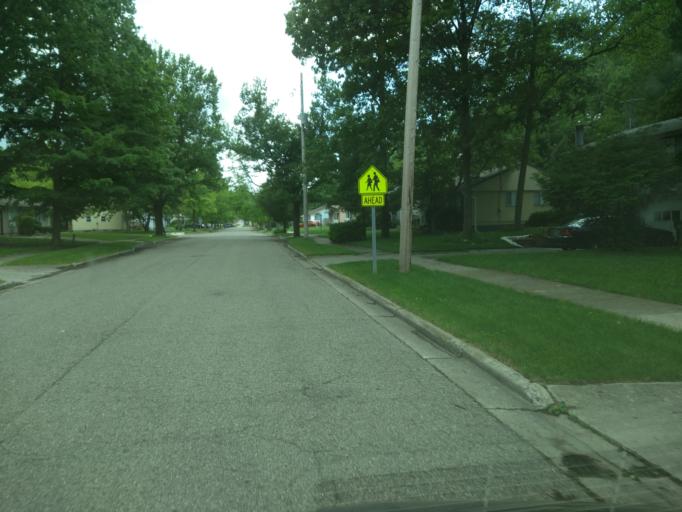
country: US
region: Michigan
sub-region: Eaton County
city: Waverly
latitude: 42.7016
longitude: -84.5964
